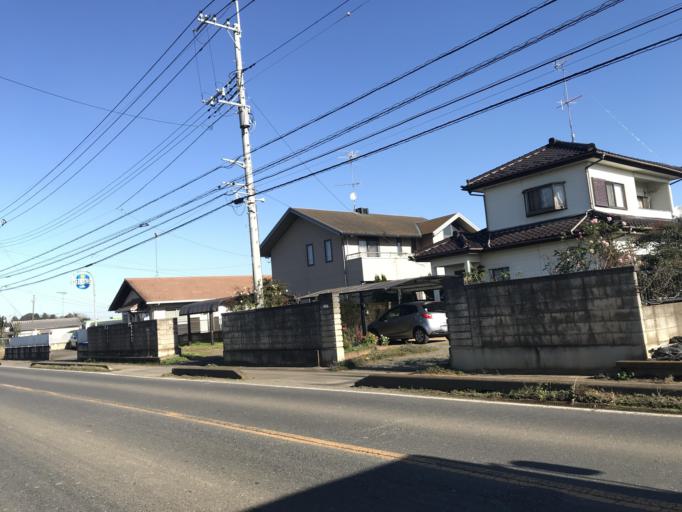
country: JP
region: Tochigi
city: Oyama
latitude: 36.2207
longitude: 139.8246
